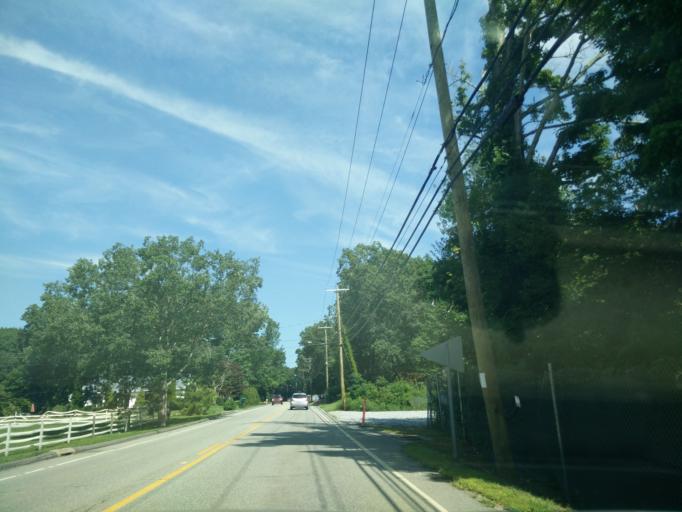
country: US
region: Connecticut
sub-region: Middlesex County
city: Clinton
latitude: 41.3014
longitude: -72.5334
